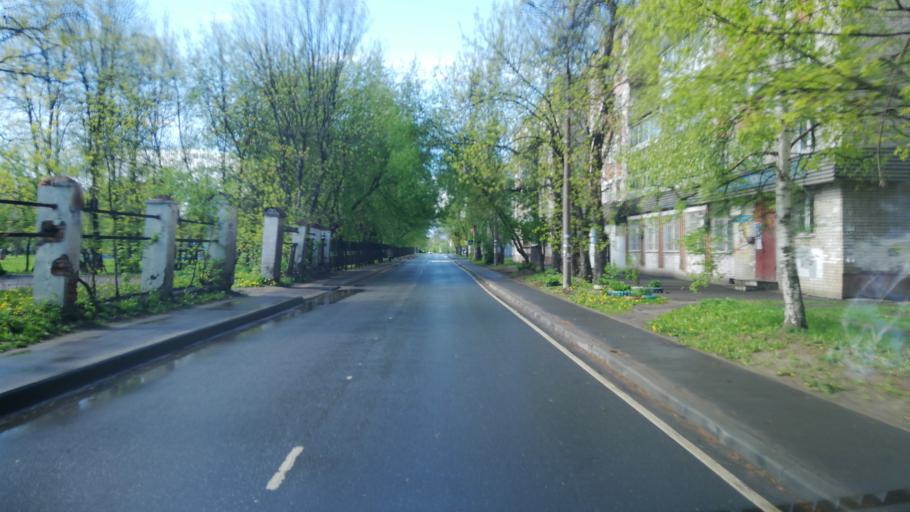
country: RU
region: Jaroslavl
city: Yaroslavl
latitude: 57.6100
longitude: 39.8264
